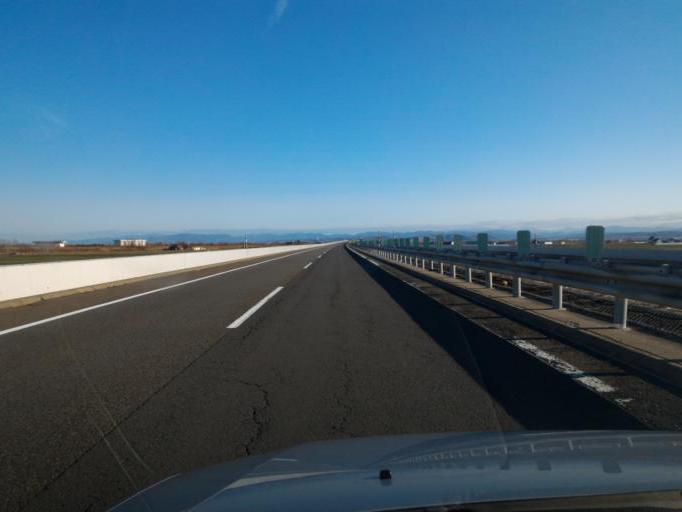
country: JP
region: Hokkaido
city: Iwamizawa
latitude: 43.1454
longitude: 141.6841
